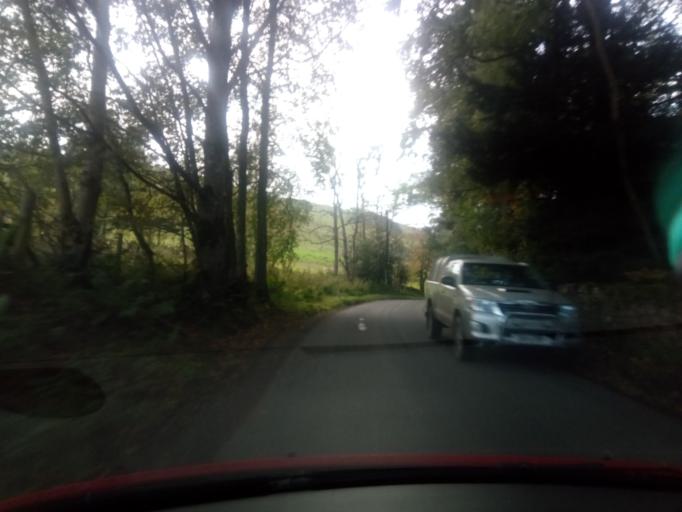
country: GB
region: Scotland
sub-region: The Scottish Borders
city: Jedburgh
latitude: 55.3761
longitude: -2.6471
